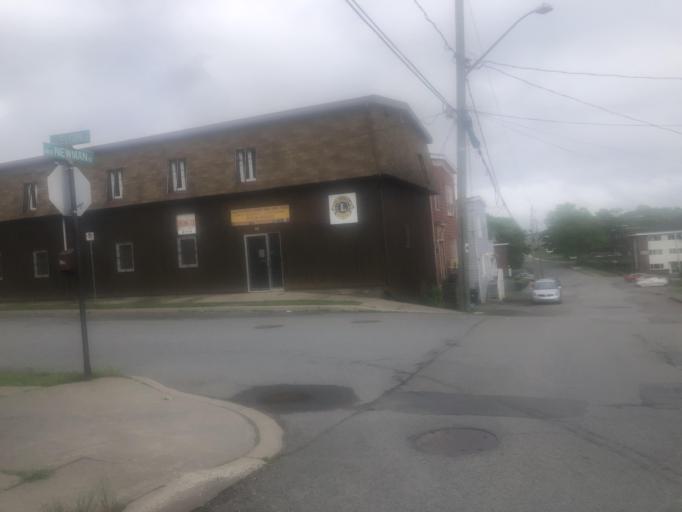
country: CA
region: New Brunswick
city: Saint John
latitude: 45.2776
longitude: -66.0831
